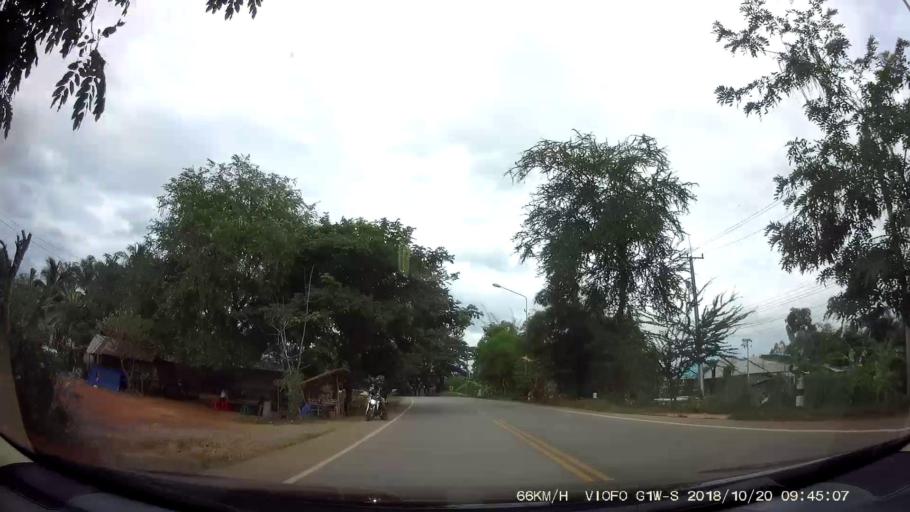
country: TH
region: Chaiyaphum
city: Khon San
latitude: 16.4895
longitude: 101.9399
